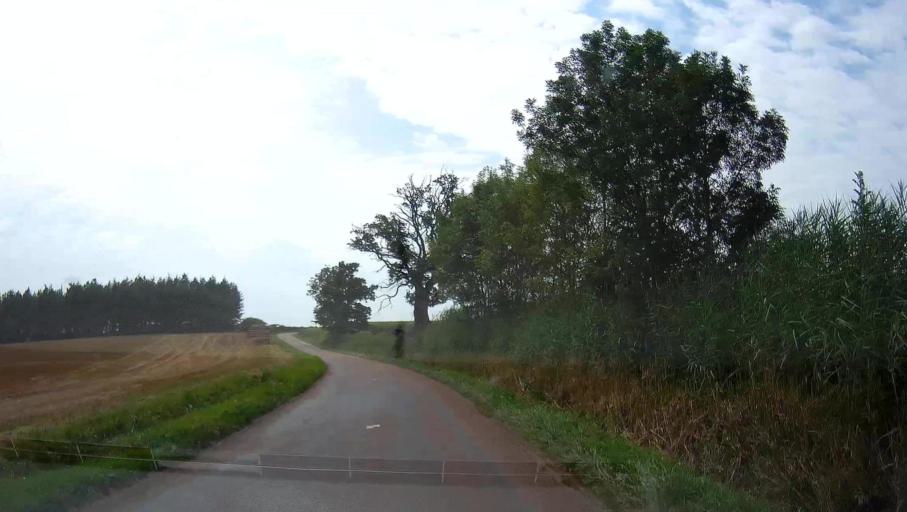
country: FR
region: Bourgogne
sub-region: Departement de Saone-et-Loire
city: Saint-Leger-sur-Dheune
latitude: 46.8853
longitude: 4.6464
